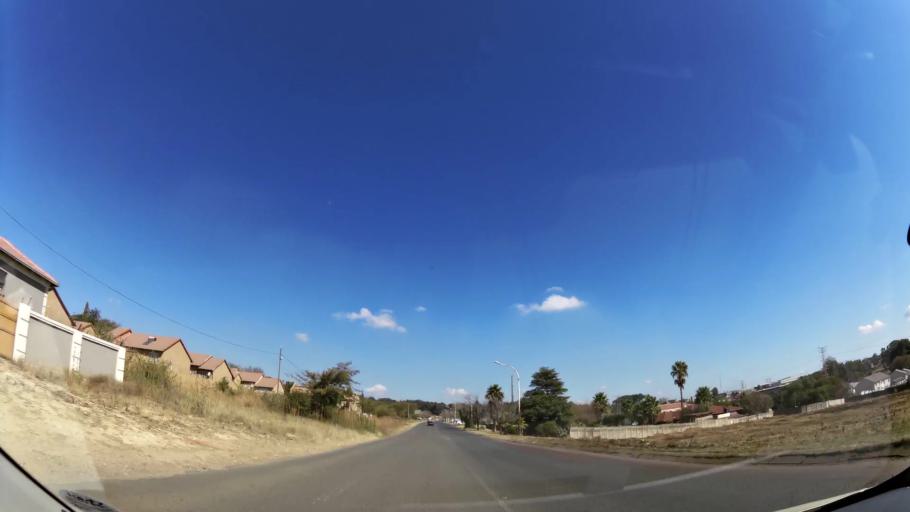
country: ZA
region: Mpumalanga
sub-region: Nkangala District Municipality
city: Witbank
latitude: -25.8572
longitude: 29.2389
